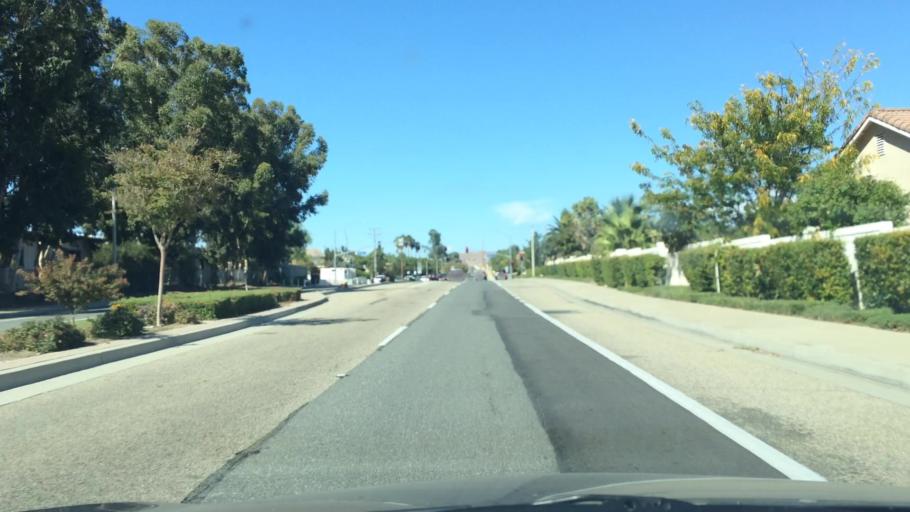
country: US
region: California
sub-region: Riverside County
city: Lake Elsinore
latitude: 33.6933
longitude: -117.3901
